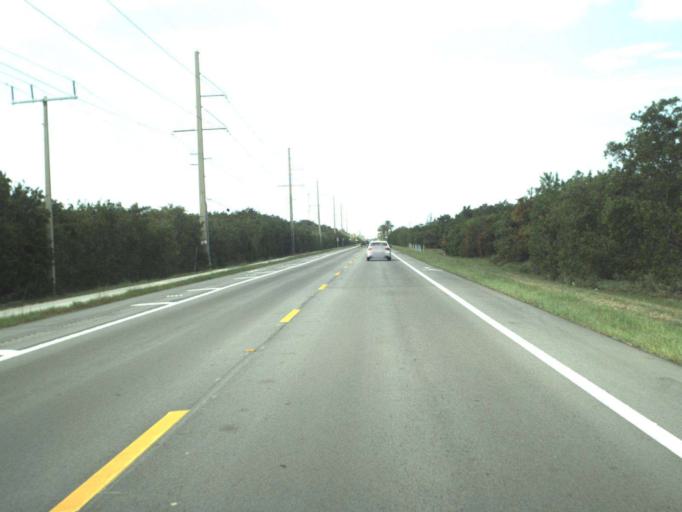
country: US
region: Florida
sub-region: Monroe County
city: Islamorada
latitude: 24.8350
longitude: -80.8021
